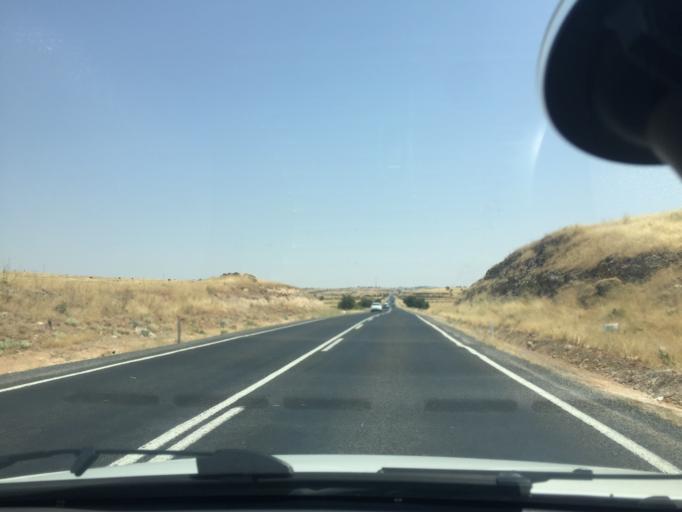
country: TR
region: Mardin
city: Kindirip
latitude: 37.4548
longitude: 41.2492
